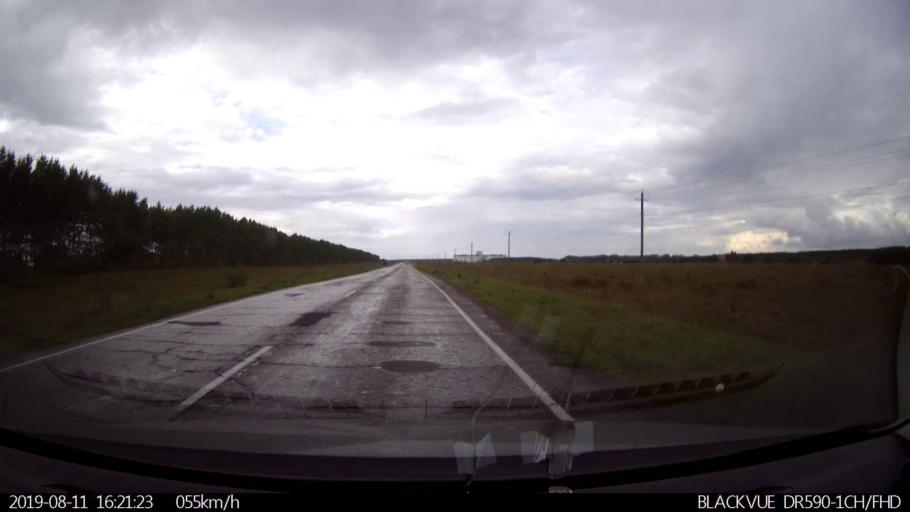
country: RU
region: Ulyanovsk
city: Mayna
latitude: 54.0795
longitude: 47.5982
